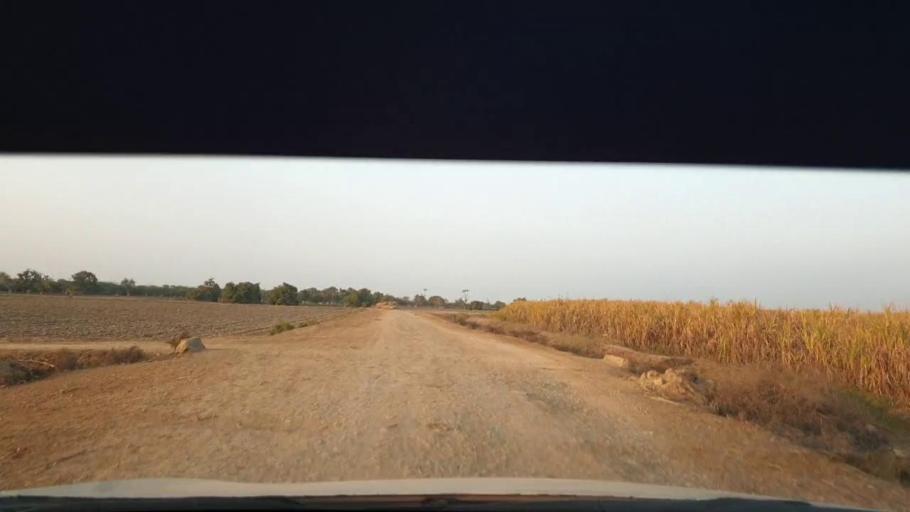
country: PK
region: Sindh
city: Berani
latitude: 25.7563
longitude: 69.0073
